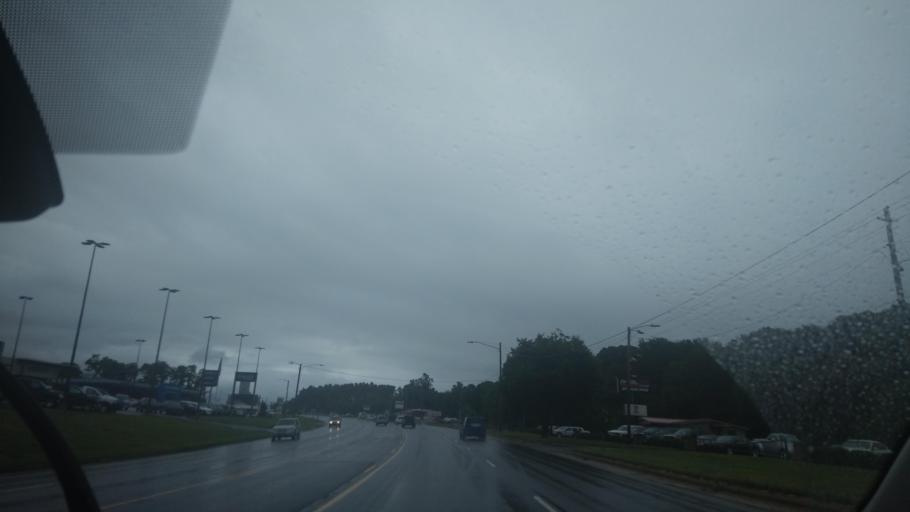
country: US
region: North Carolina
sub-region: Buncombe County
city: Bent Creek
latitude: 35.5613
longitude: -82.6322
